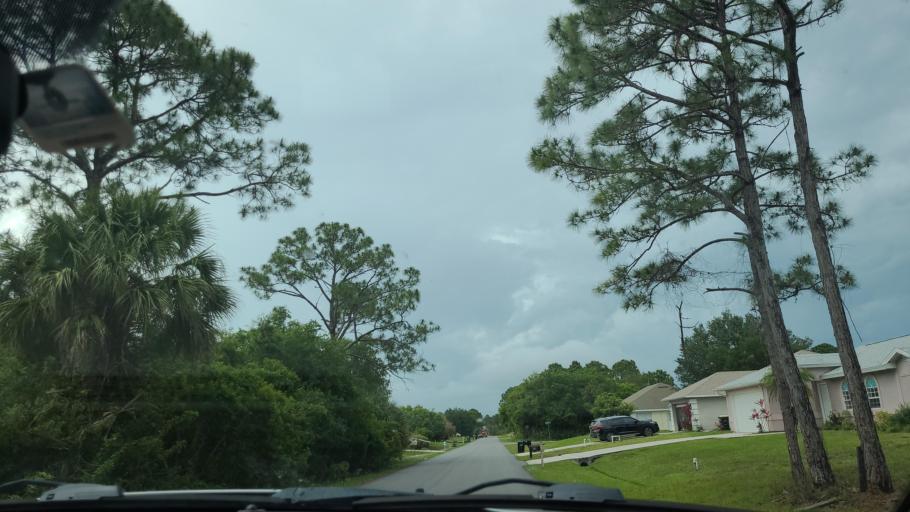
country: US
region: Florida
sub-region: Brevard County
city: Grant-Valkaria
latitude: 27.9455
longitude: -80.6306
